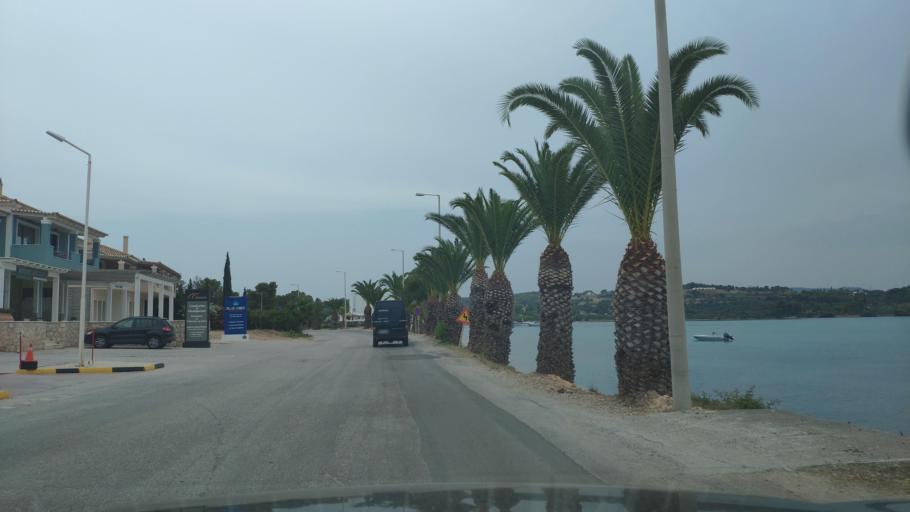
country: GR
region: Peloponnese
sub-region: Nomos Argolidos
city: Porto Cheli
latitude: 37.3220
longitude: 23.1567
